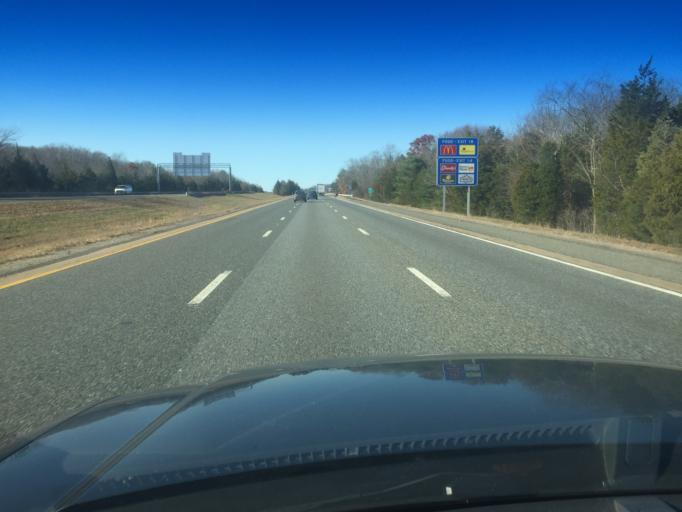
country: US
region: Massachusetts
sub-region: Bristol County
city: Attleboro
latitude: 41.9535
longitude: -71.3194
